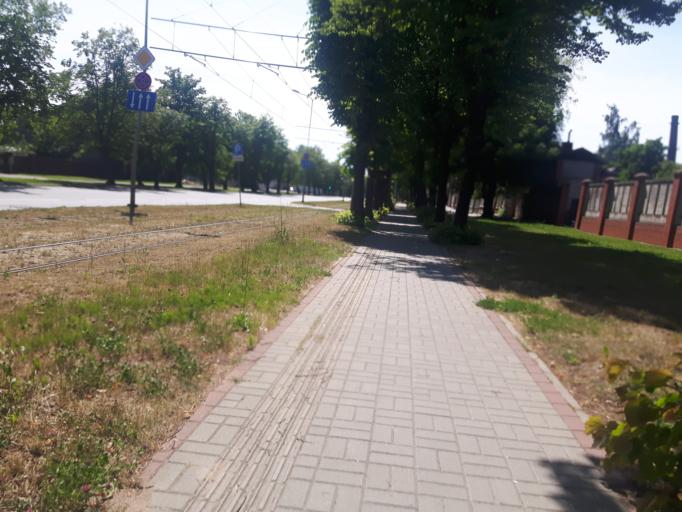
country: LV
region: Liepaja
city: Vec-Liepaja
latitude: 56.5252
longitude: 21.0294
